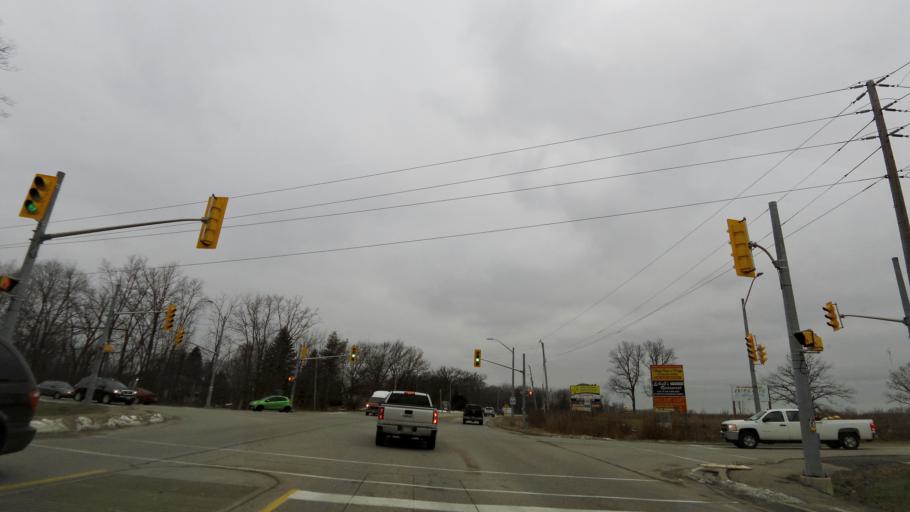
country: CA
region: Ontario
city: Ancaster
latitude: 43.1015
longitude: -80.0948
